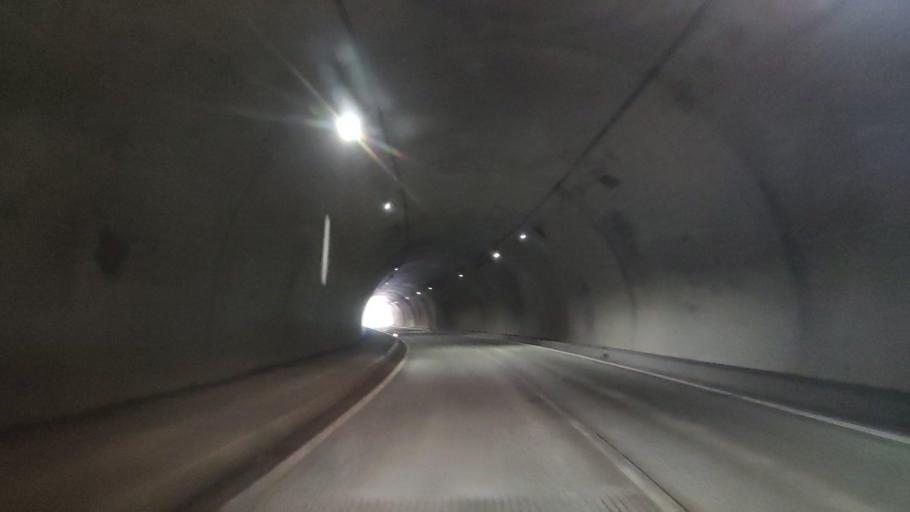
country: JP
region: Gifu
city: Takayama
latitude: 36.3354
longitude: 137.3019
